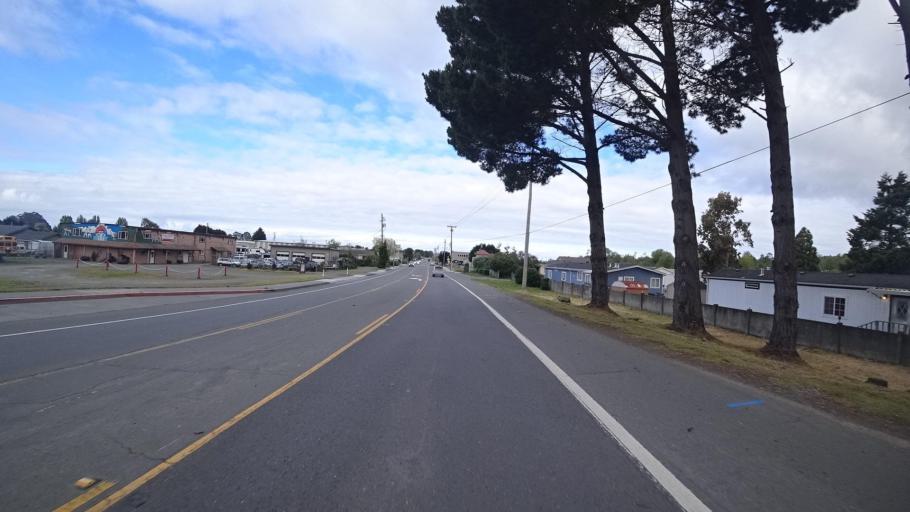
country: US
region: California
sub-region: Humboldt County
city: Arcata
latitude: 40.9050
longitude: -124.0757
